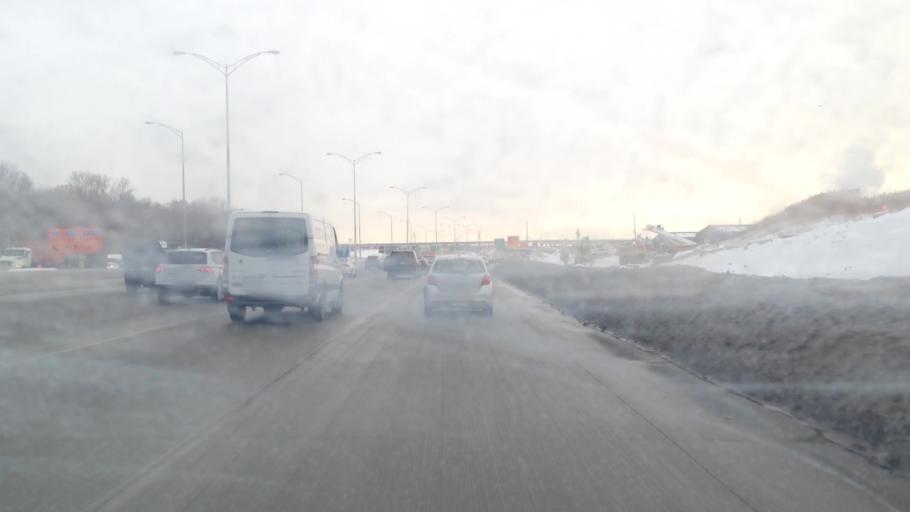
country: CA
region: Quebec
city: Saint-Raymond
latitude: 45.4598
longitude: -73.6182
